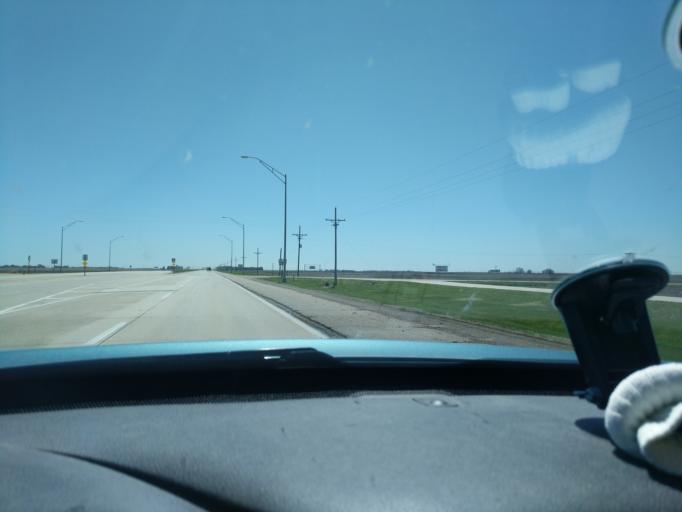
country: US
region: Nebraska
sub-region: Thayer County
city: Hebron
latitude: 40.3226
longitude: -97.5768
